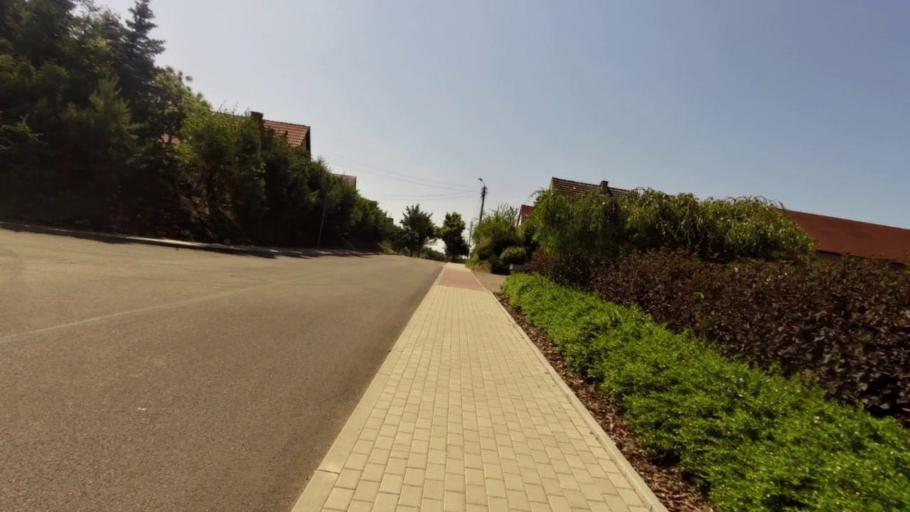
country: PL
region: West Pomeranian Voivodeship
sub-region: Powiat swidwinski
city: Polczyn-Zdroj
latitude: 53.7752
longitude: 16.1080
